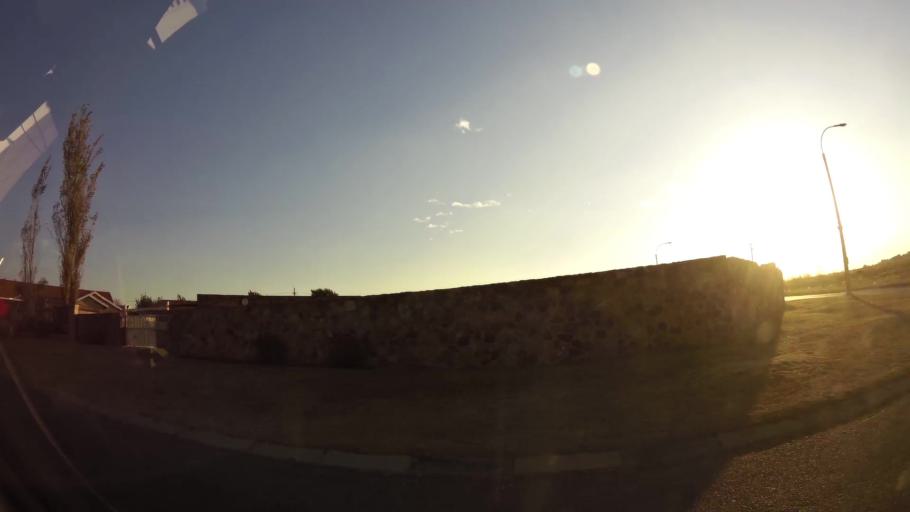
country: ZA
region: Gauteng
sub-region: West Rand District Municipality
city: Randfontein
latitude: -26.2024
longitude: 27.6564
